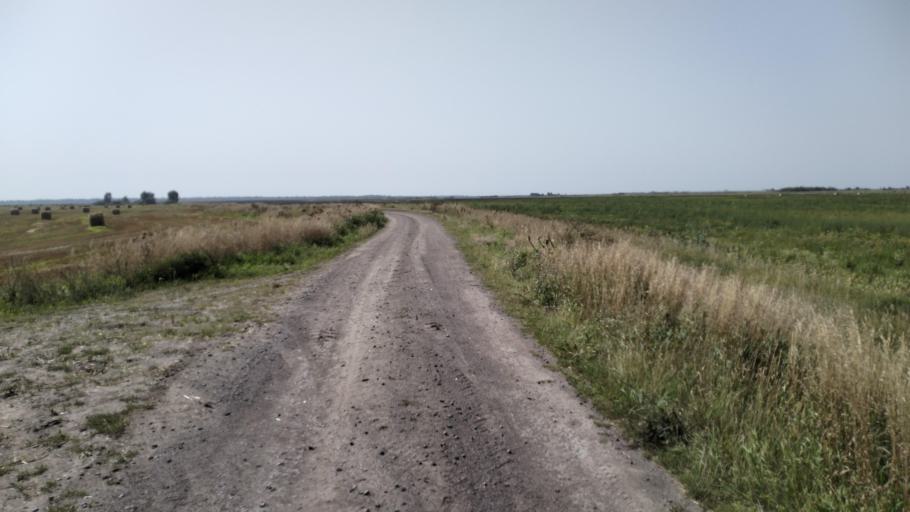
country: BY
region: Brest
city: Davyd-Haradok
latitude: 52.0042
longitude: 27.1657
